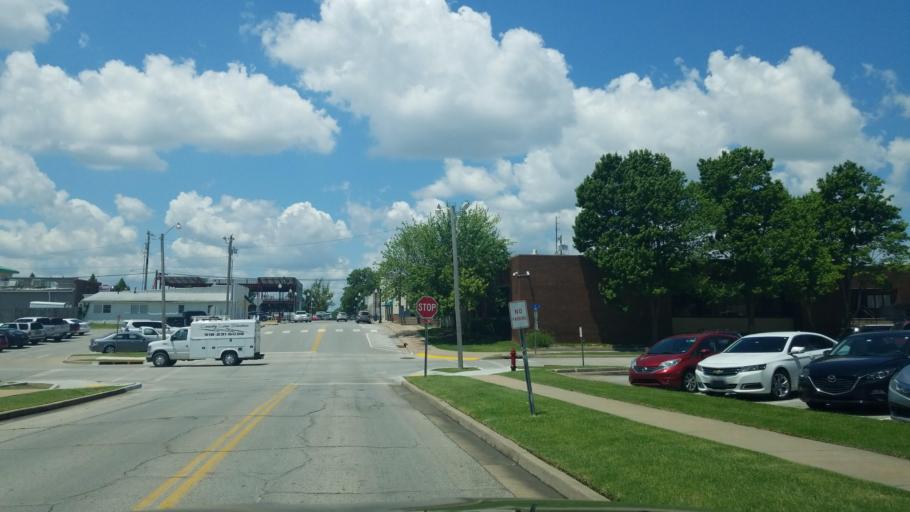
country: US
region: Oklahoma
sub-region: Tulsa County
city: Broken Arrow
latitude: 36.0504
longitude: -95.7891
